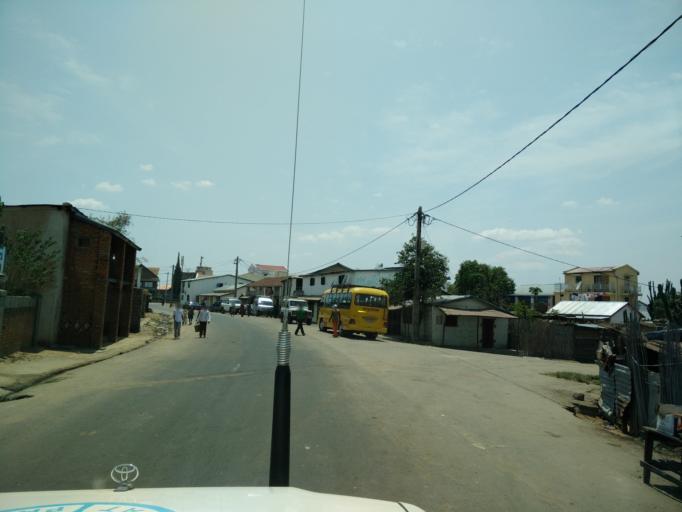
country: MG
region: Ihorombe
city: Ranohira
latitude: -22.5580
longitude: 45.4139
